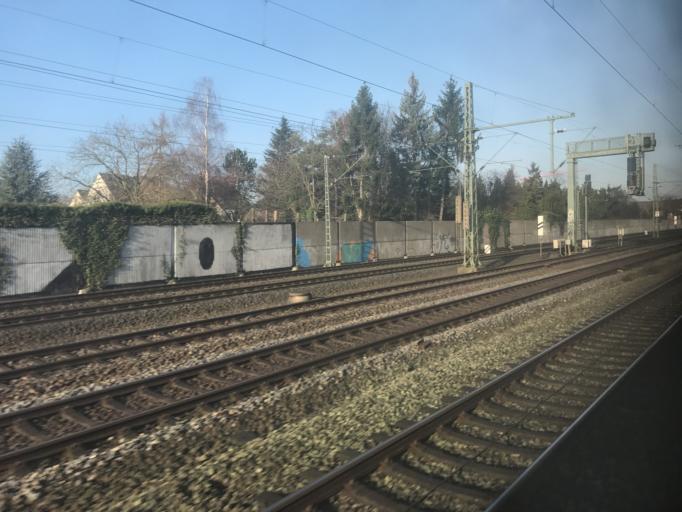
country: DE
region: North Rhine-Westphalia
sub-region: Regierungsbezirk Dusseldorf
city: Dusseldorf
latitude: 51.2706
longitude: 6.7895
